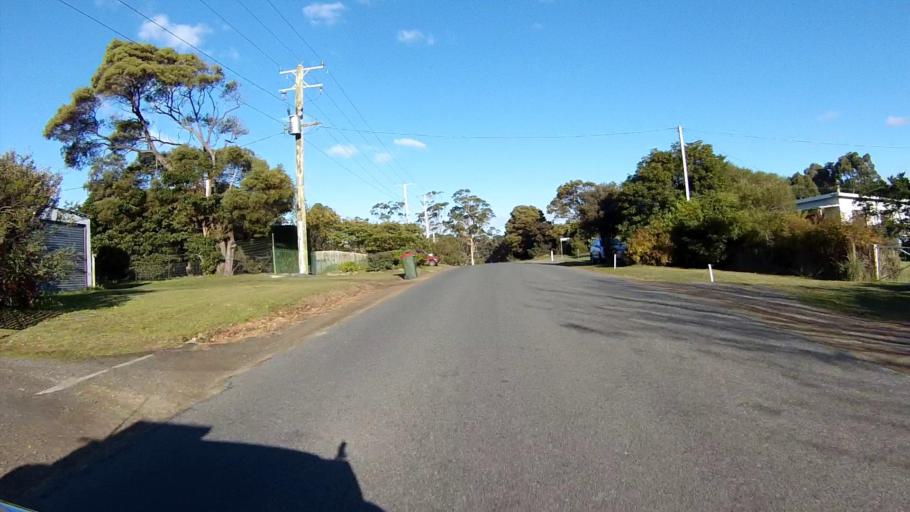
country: AU
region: Tasmania
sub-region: Clarence
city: Sandford
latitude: -43.1602
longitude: 147.8537
